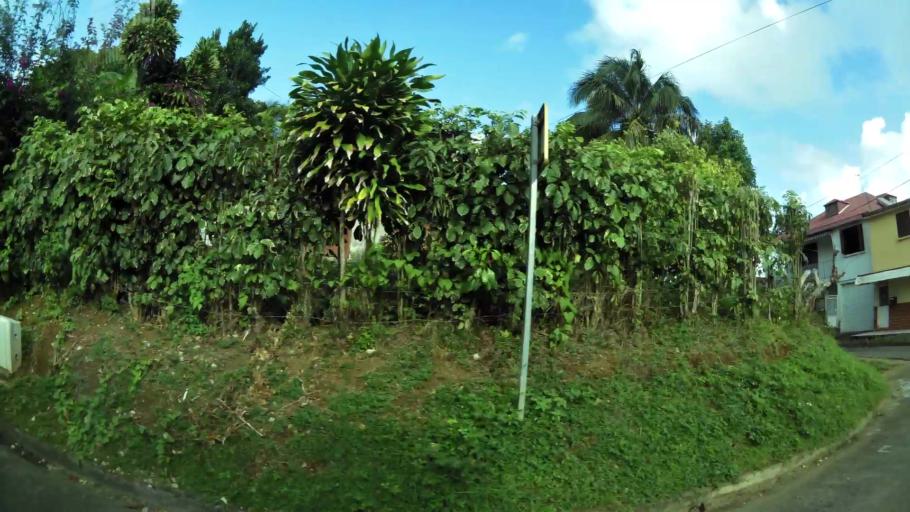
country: GP
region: Guadeloupe
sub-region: Guadeloupe
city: Les Abymes
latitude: 16.2524
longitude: -61.5113
